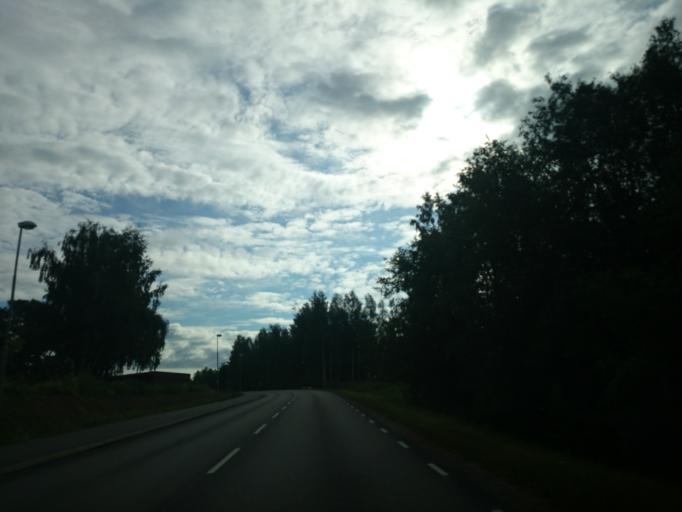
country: SE
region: Vaesternorrland
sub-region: Sundsvalls Kommun
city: Johannedal
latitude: 62.4320
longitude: 17.3808
